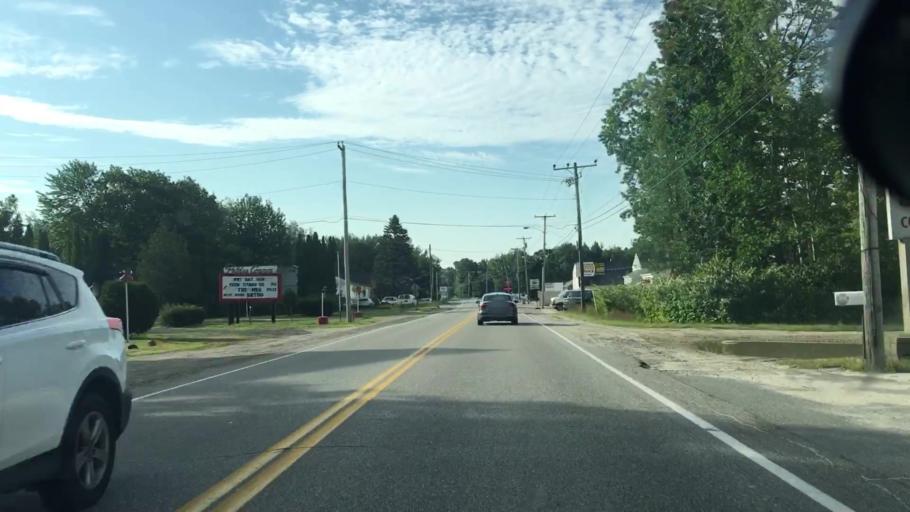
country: US
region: Maine
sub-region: Cumberland County
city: Westbrook
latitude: 43.7243
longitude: -70.3409
